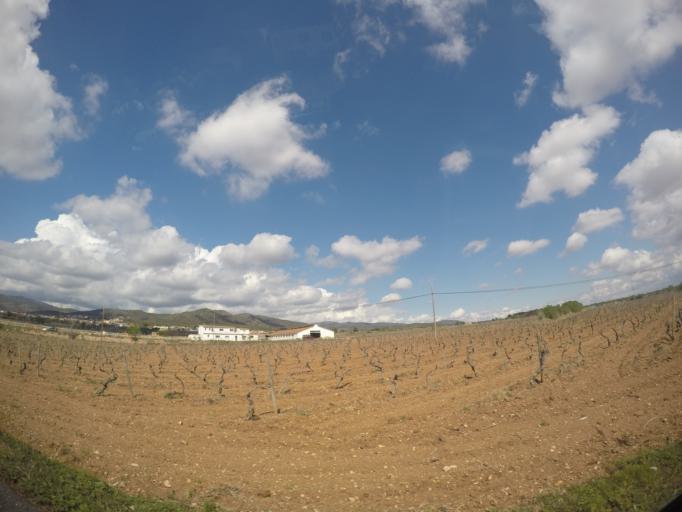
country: ES
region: Catalonia
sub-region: Provincia de Tarragona
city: Santa Oliva
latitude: 41.2839
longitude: 1.5291
